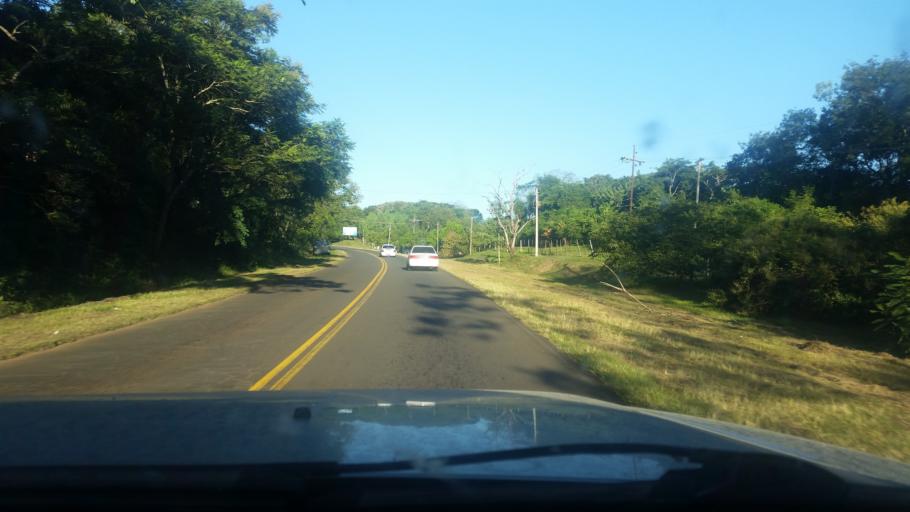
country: PY
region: Guaira
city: Independencia
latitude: -25.7175
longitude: -56.2756
